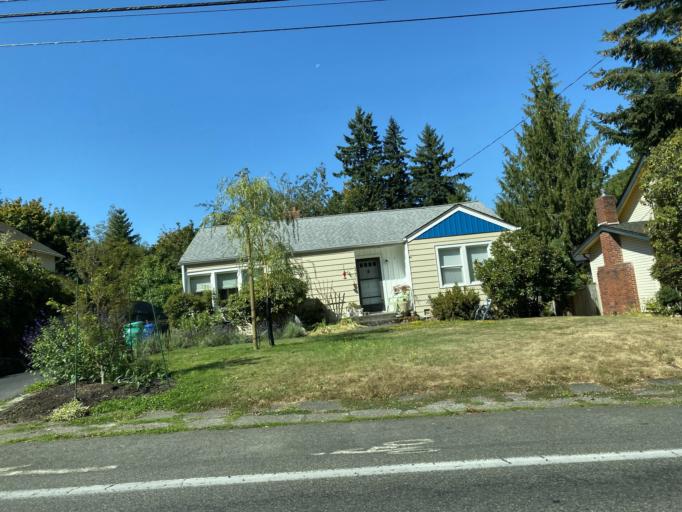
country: US
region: Washington
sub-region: Thurston County
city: Olympia
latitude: 47.0335
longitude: -122.8868
